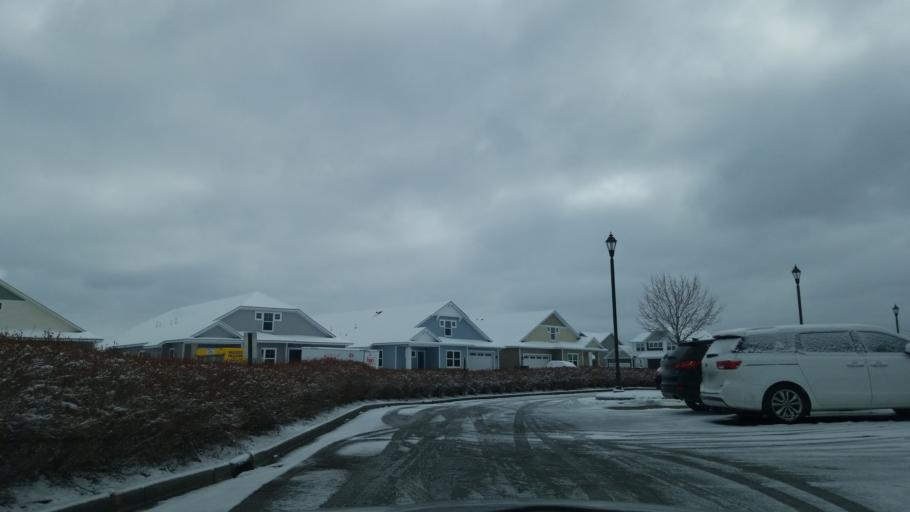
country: US
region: Wisconsin
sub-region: Saint Croix County
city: Hudson
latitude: 44.9504
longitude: -92.6997
